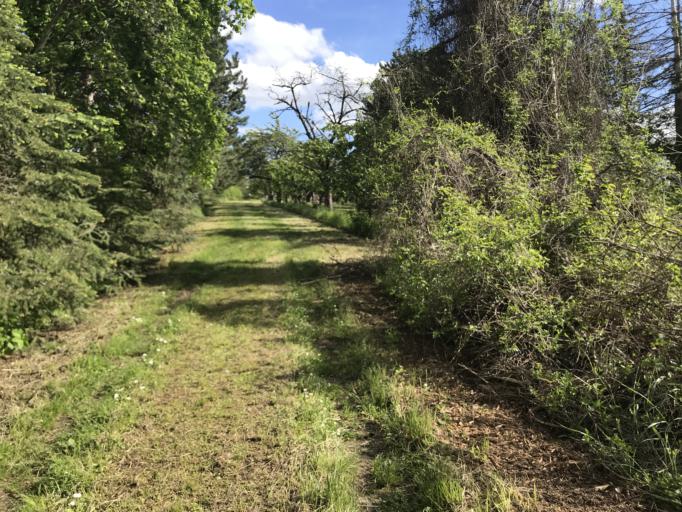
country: DE
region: Rheinland-Pfalz
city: Wackernheim
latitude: 49.9696
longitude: 8.1164
